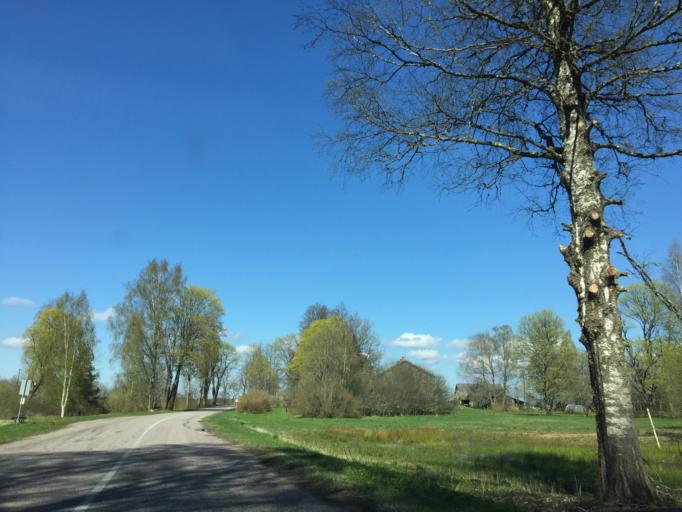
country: LV
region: Strenci
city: Seda
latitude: 57.5576
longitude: 25.8254
